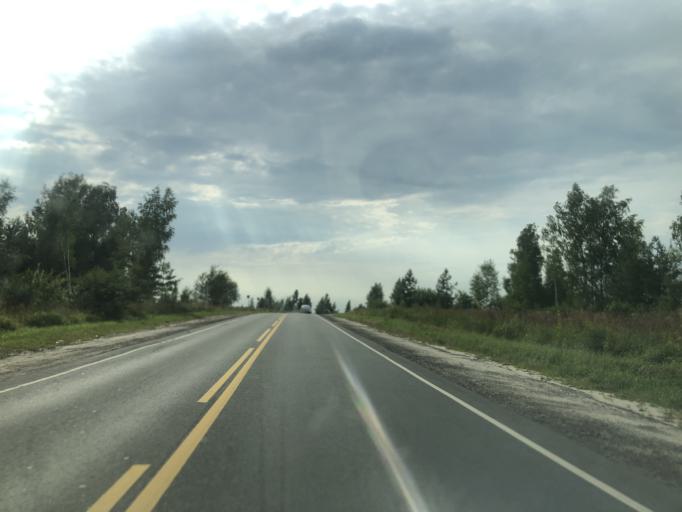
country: RU
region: Ivanovo
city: Shuya
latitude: 56.8580
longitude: 41.4806
